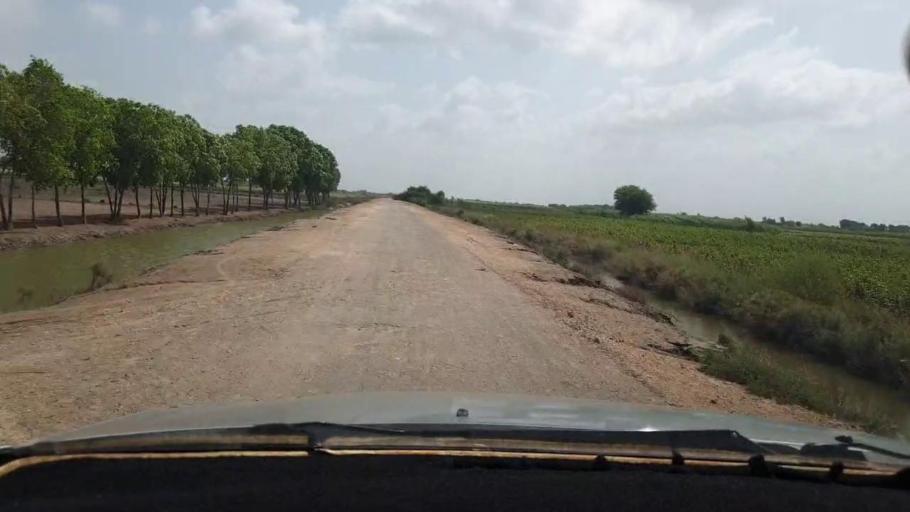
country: PK
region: Sindh
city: Tando Bago
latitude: 24.7207
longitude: 69.1799
